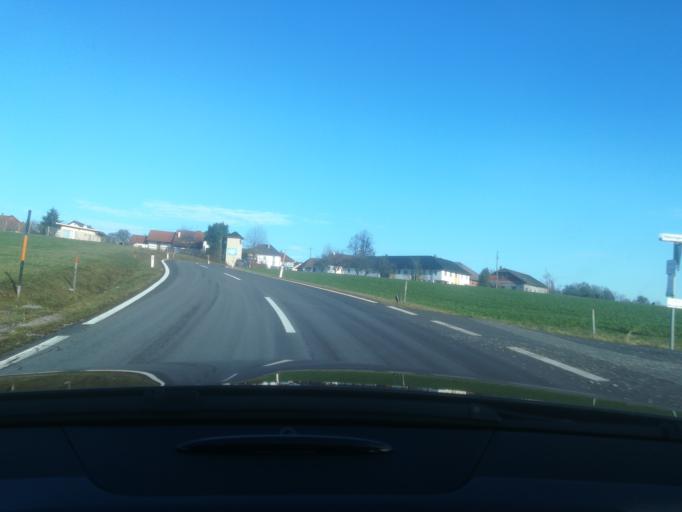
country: AT
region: Upper Austria
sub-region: Politischer Bezirk Urfahr-Umgebung
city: Herzogsdorf
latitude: 48.4261
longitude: 14.1088
